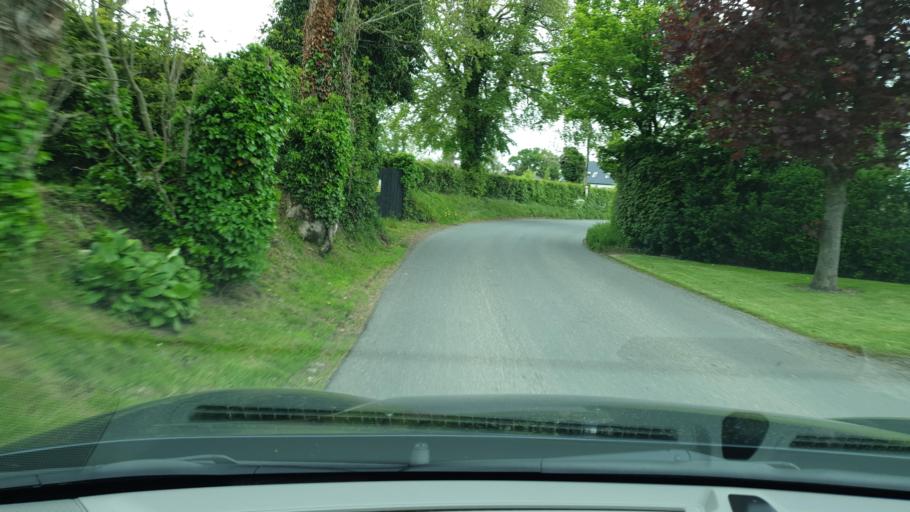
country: IE
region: Leinster
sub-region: An Mhi
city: Ratoath
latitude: 53.4830
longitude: -6.5021
